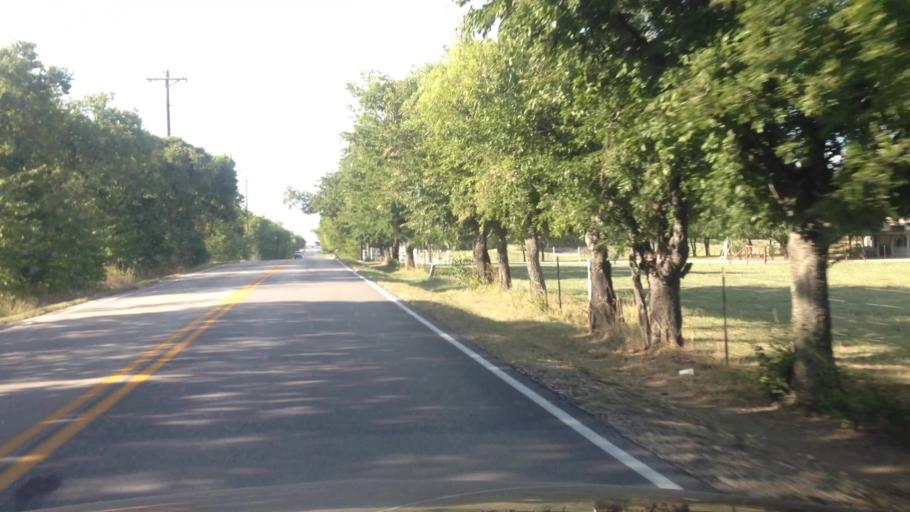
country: US
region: Texas
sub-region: Tarrant County
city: Haslet
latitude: 32.9319
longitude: -97.3920
